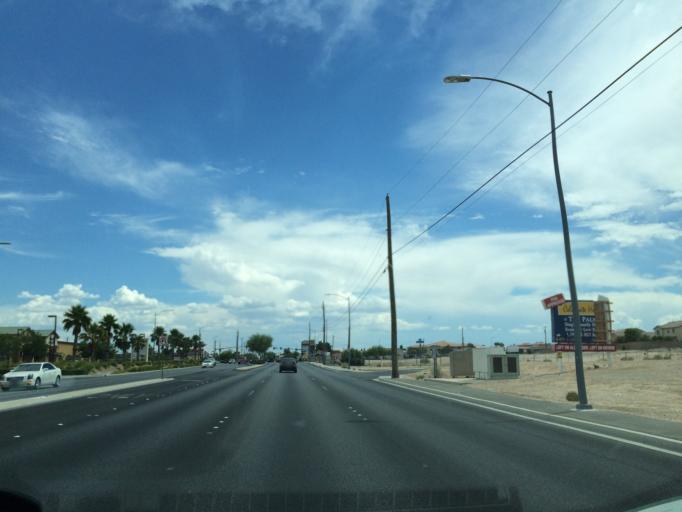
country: US
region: Nevada
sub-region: Clark County
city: North Las Vegas
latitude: 36.2345
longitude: -115.1621
